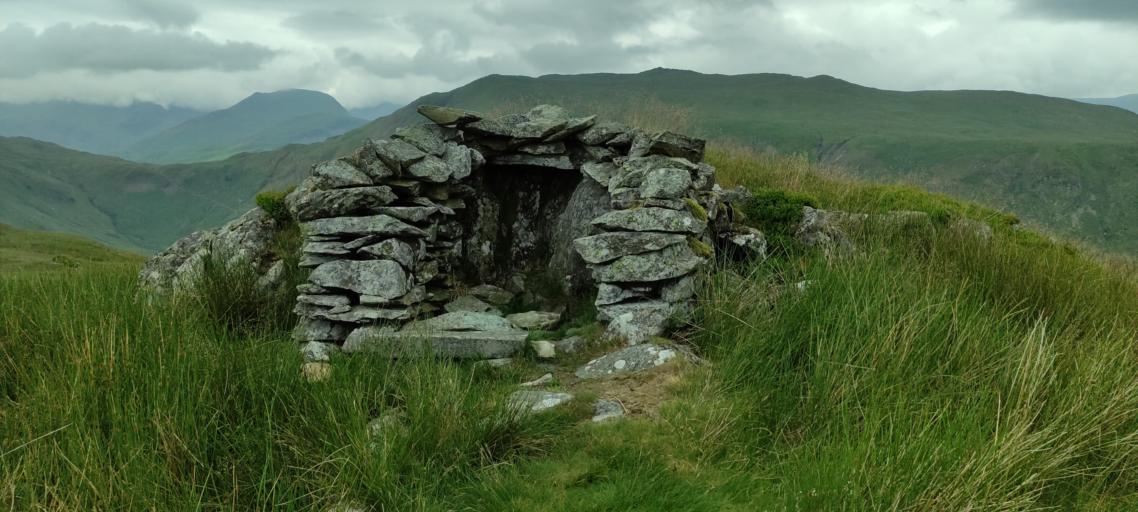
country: GB
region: England
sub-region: Cumbria
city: Ambleside
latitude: 54.5479
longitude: -2.8857
